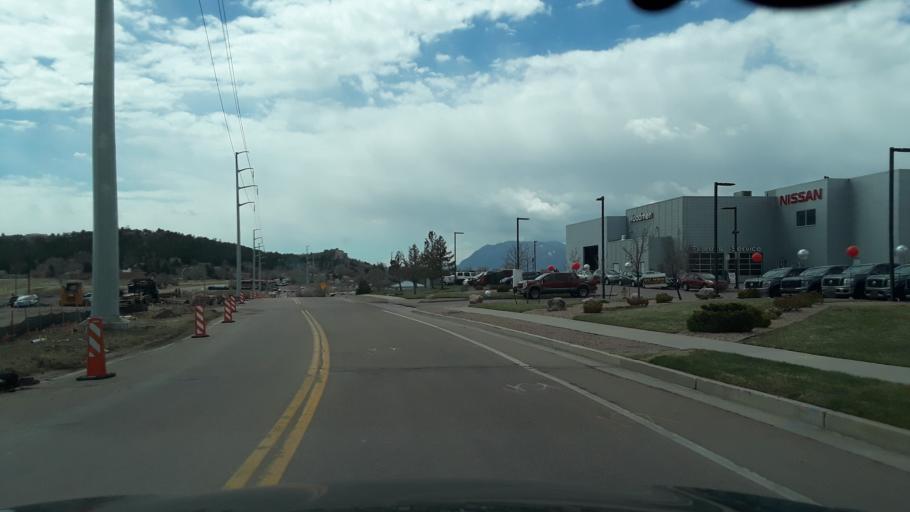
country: US
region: Colorado
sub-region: El Paso County
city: Air Force Academy
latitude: 38.9316
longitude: -104.8109
